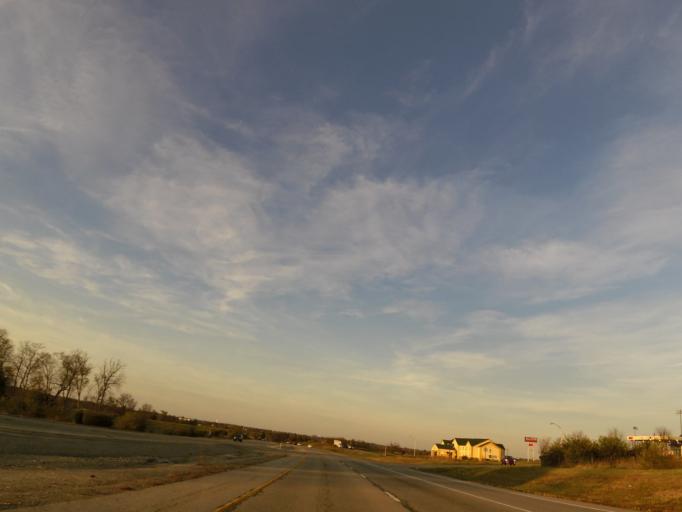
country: US
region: Kentucky
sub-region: Jessamine County
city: Nicholasville
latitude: 37.8344
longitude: -84.5862
